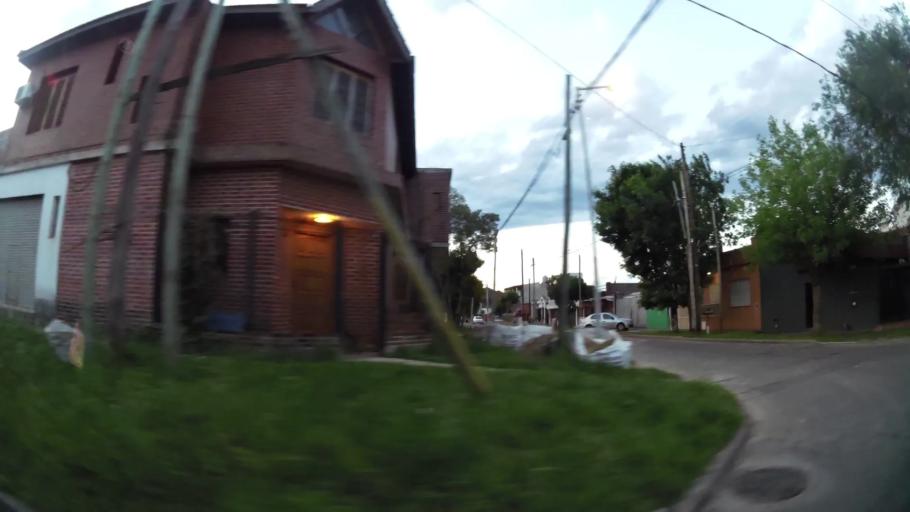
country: AR
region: Buenos Aires
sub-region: Partido de Avellaneda
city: Avellaneda
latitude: -34.6827
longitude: -58.3358
